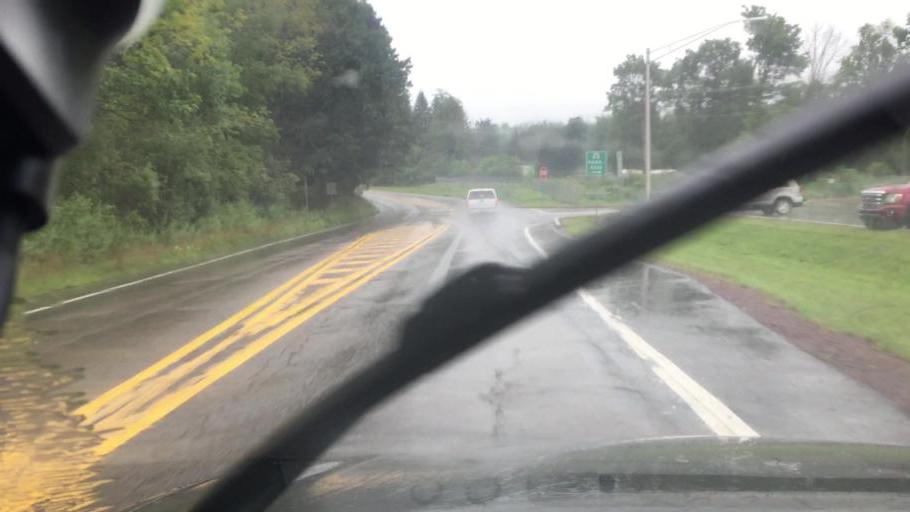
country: US
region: Pennsylvania
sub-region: Luzerne County
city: White Haven
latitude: 41.0481
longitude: -75.7776
